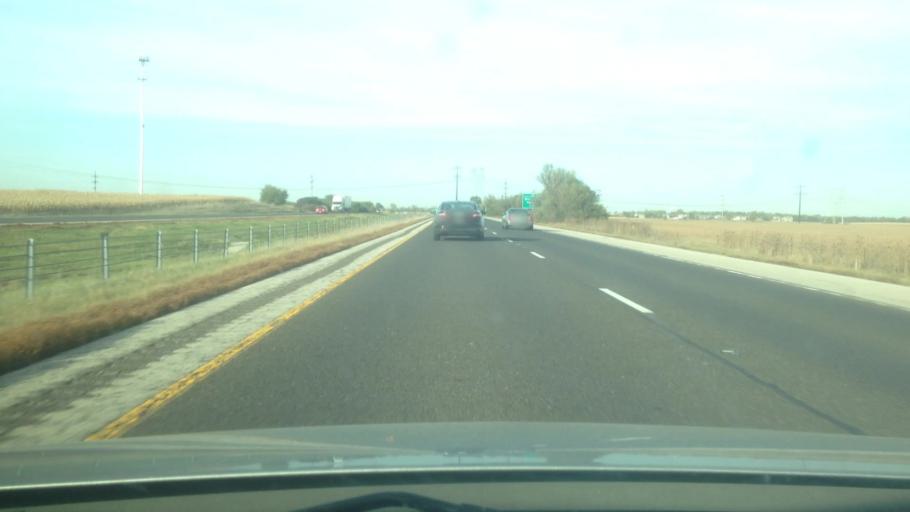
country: US
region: Illinois
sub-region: Will County
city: Peotone
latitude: 41.3068
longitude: -87.8250
